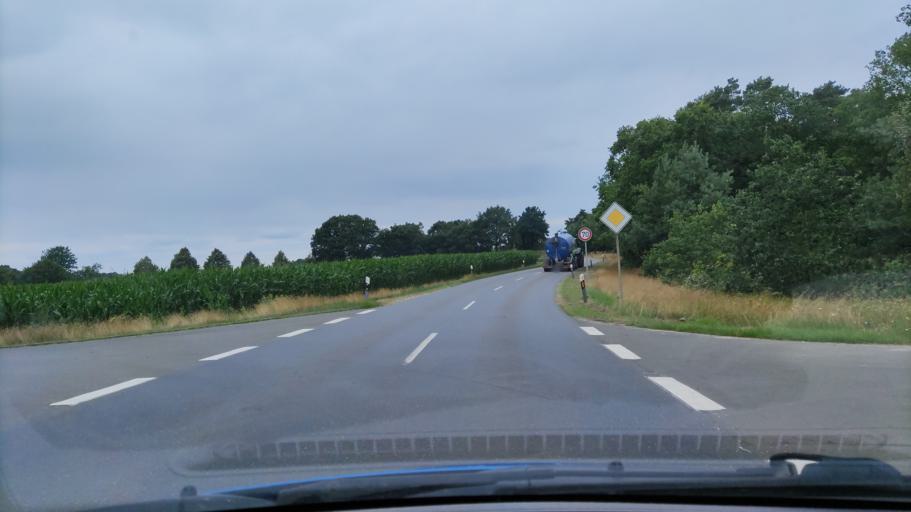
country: DE
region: Lower Saxony
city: Rosche
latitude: 53.0020
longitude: 10.7677
